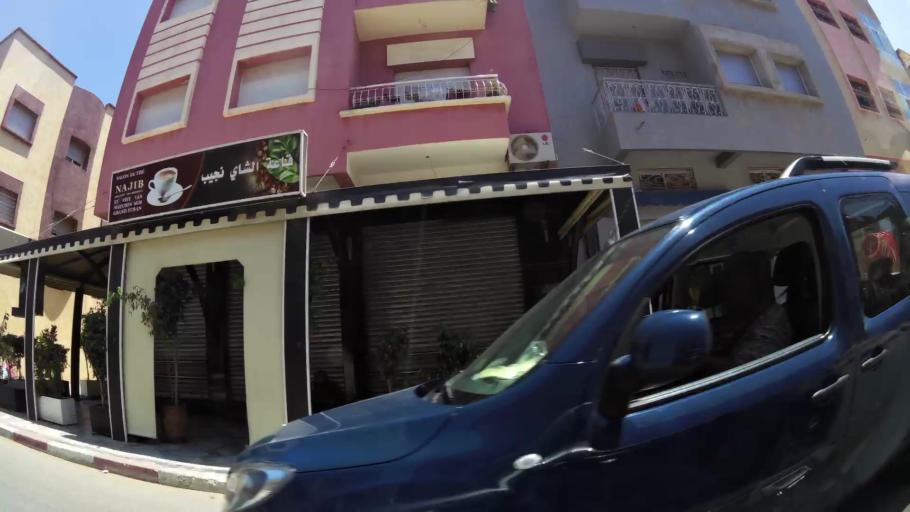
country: MA
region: Gharb-Chrarda-Beni Hssen
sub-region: Kenitra Province
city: Kenitra
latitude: 34.2631
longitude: -6.6436
